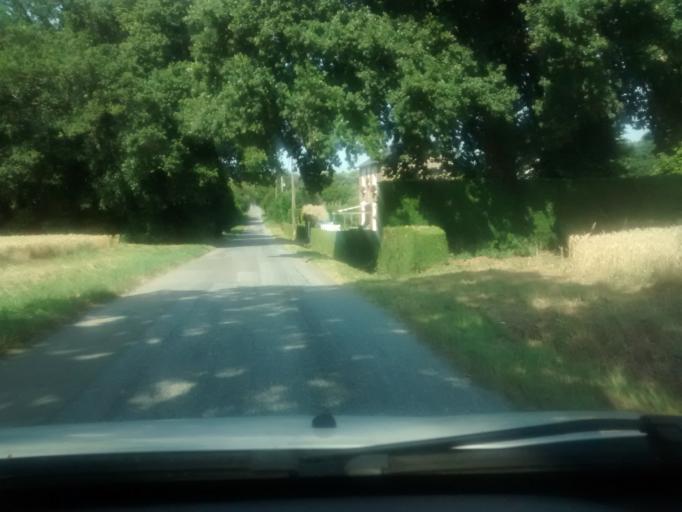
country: FR
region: Brittany
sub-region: Departement d'Ille-et-Vilaine
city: Cesson-Sevigne
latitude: 48.1313
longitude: -1.6012
